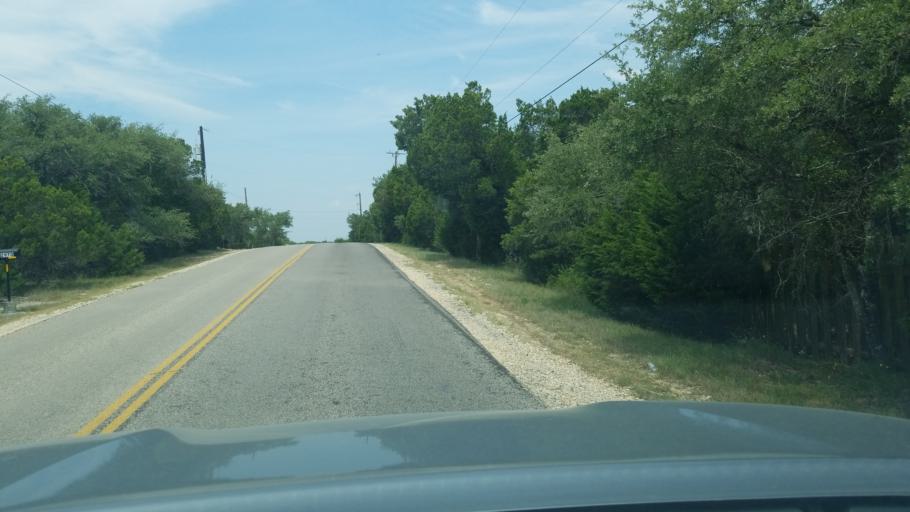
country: US
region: Texas
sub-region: Comal County
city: Bulverde
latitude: 29.7758
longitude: -98.4385
